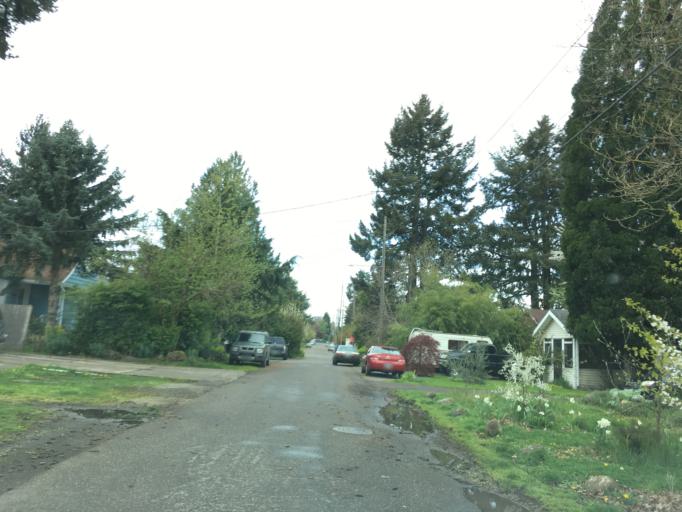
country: US
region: Oregon
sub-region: Multnomah County
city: Lents
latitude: 45.5497
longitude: -122.5995
